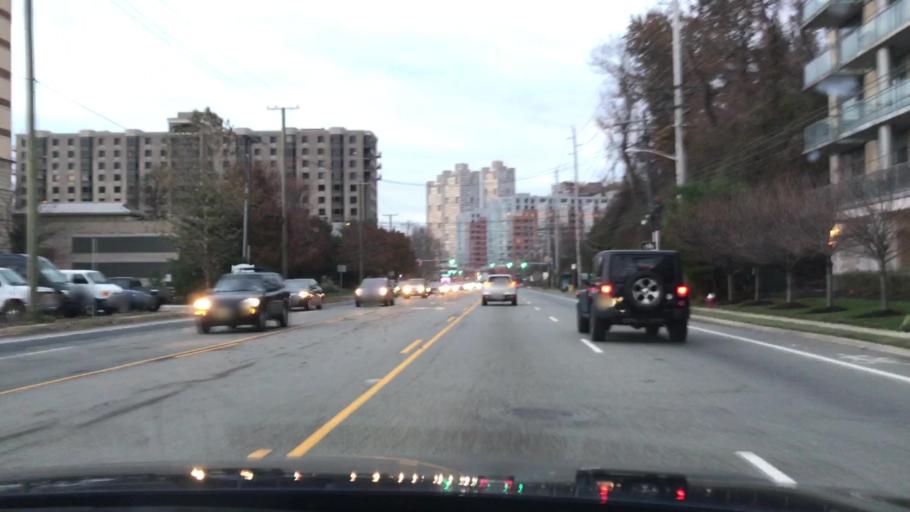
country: US
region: New Jersey
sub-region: Hudson County
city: Guttenberg
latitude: 40.7990
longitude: -73.9949
